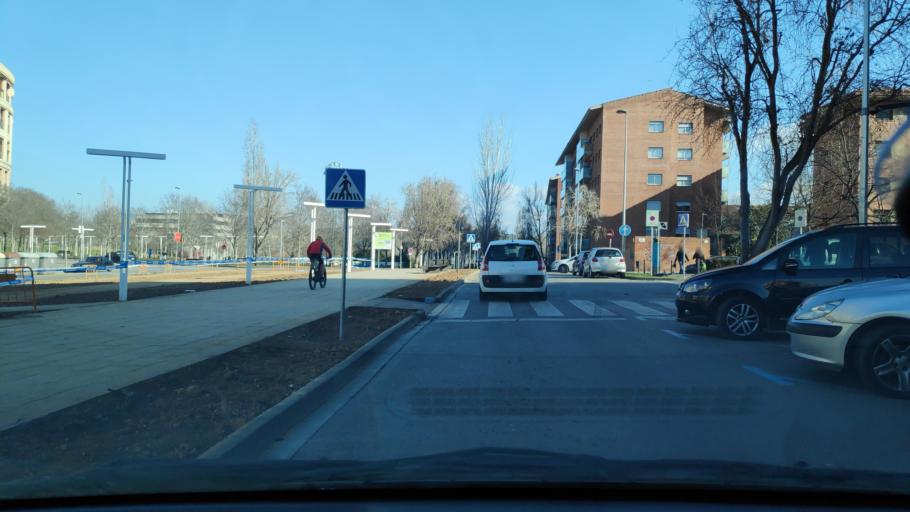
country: ES
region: Catalonia
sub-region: Provincia de Barcelona
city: Sant Cugat del Valles
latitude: 41.4718
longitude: 2.0917
